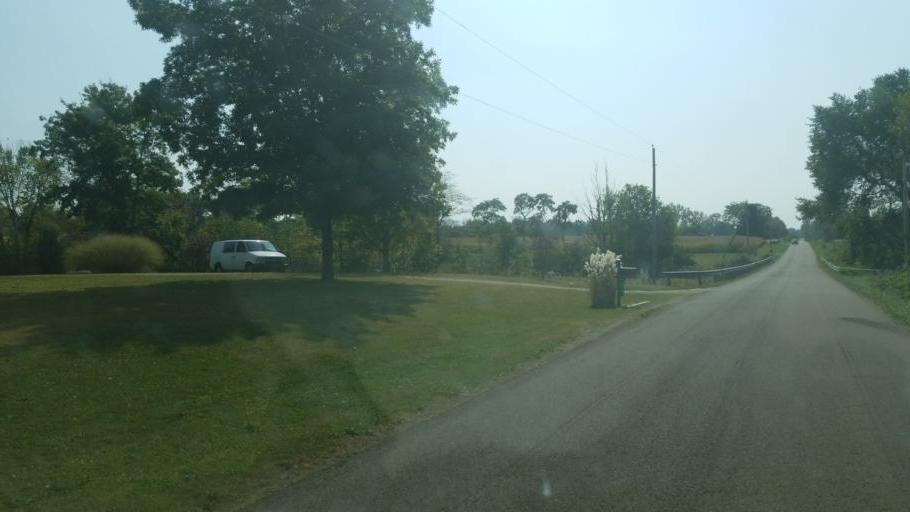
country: US
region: Ohio
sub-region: Morrow County
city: Mount Gilead
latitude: 40.5812
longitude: -82.8431
